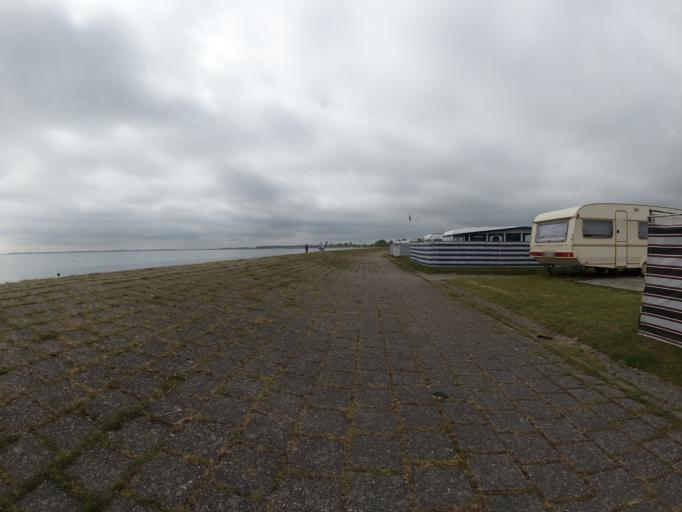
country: DE
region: Lower Saxony
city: Schillig
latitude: 53.6964
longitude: 8.0280
